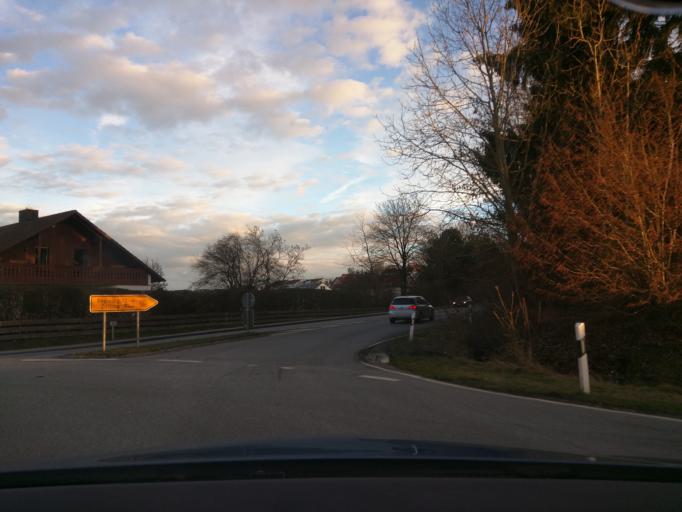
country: DE
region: Bavaria
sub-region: Upper Bavaria
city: Attenkirchen
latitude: 48.5093
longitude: 11.7571
